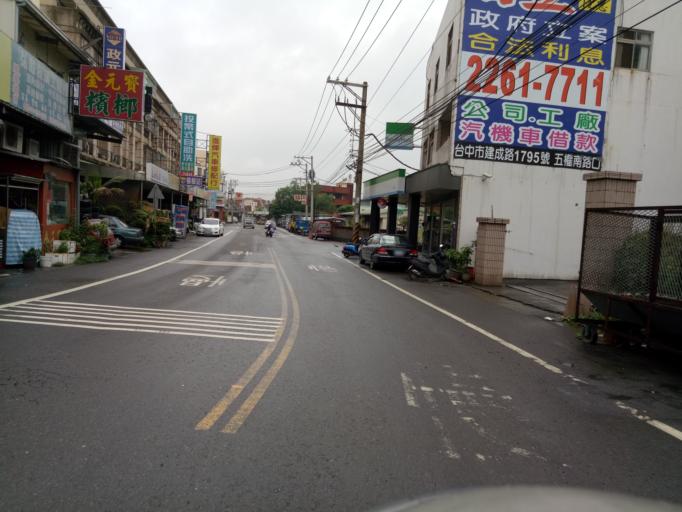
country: TW
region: Taiwan
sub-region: Taichung City
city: Taichung
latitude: 24.1118
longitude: 120.7072
